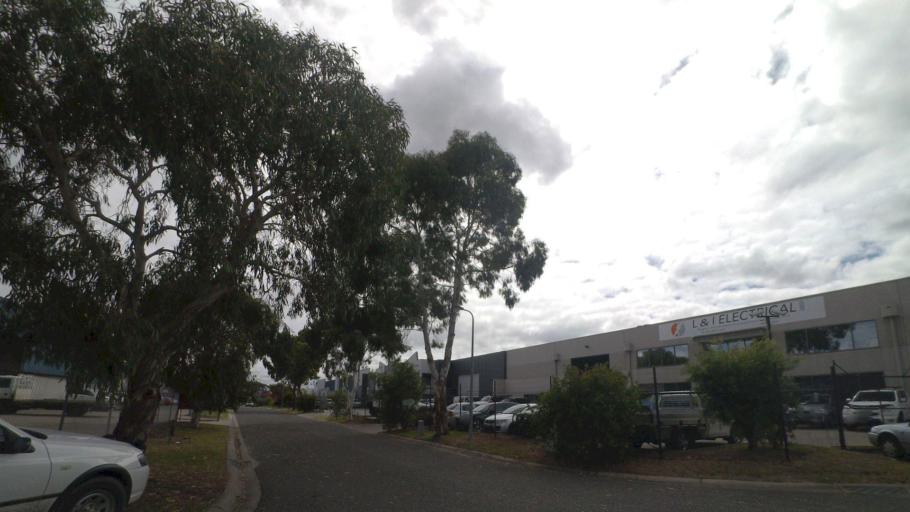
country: AU
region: Victoria
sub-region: Maroondah
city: Bayswater North
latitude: -37.8237
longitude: 145.3072
